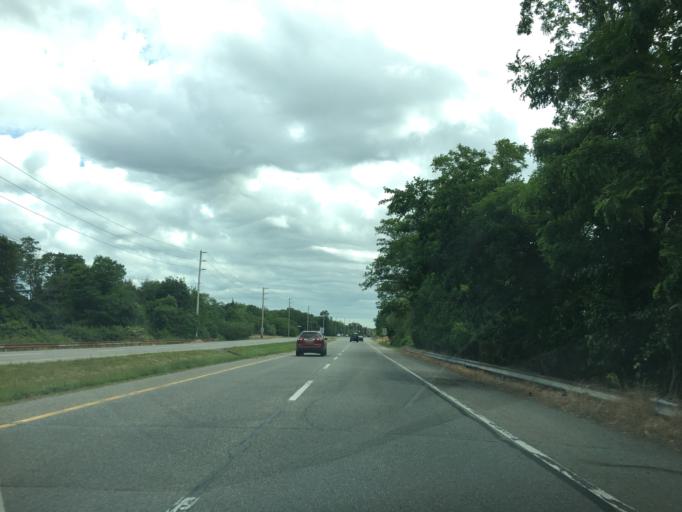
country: US
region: New York
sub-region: Suffolk County
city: Mattituck
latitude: 40.9990
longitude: -72.5301
